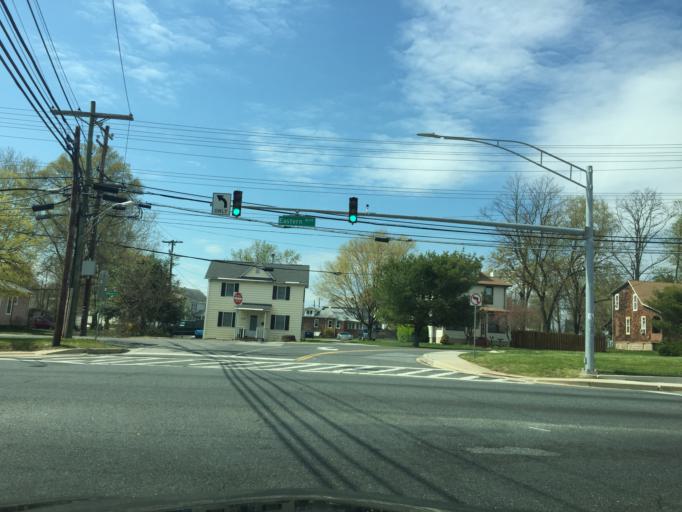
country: US
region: Maryland
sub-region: Baltimore County
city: Middle River
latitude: 39.3290
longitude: -76.4406
